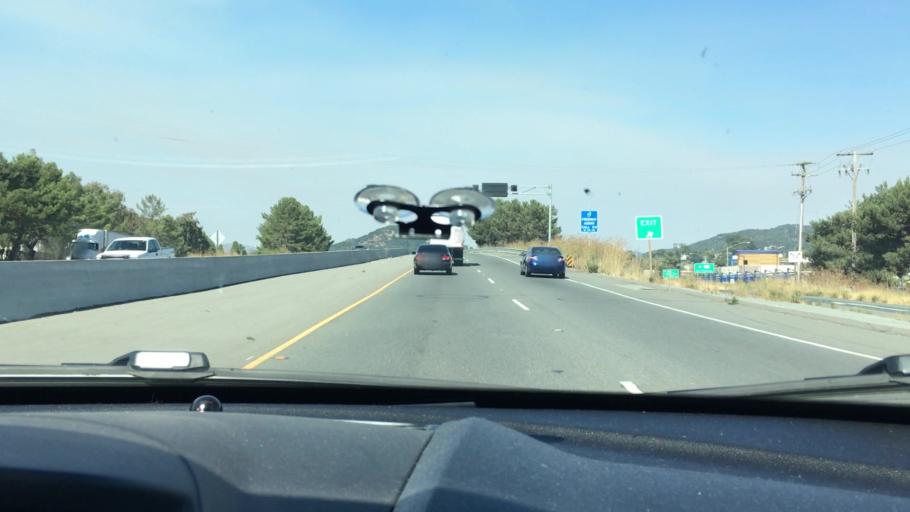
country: US
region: California
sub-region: Marin County
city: San Rafael
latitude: 37.9585
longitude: -122.5038
